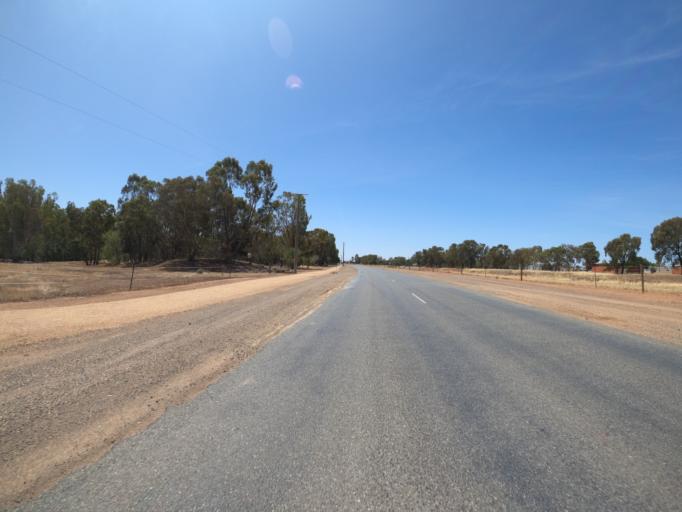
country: AU
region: Victoria
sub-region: Moira
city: Yarrawonga
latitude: -36.0160
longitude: 145.9960
